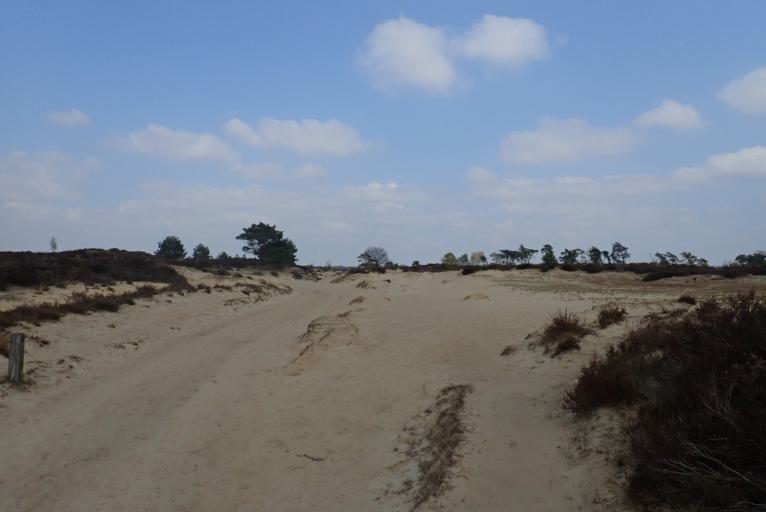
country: BE
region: Flanders
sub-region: Provincie Antwerpen
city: Kalmthout
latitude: 51.3994
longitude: 4.4254
